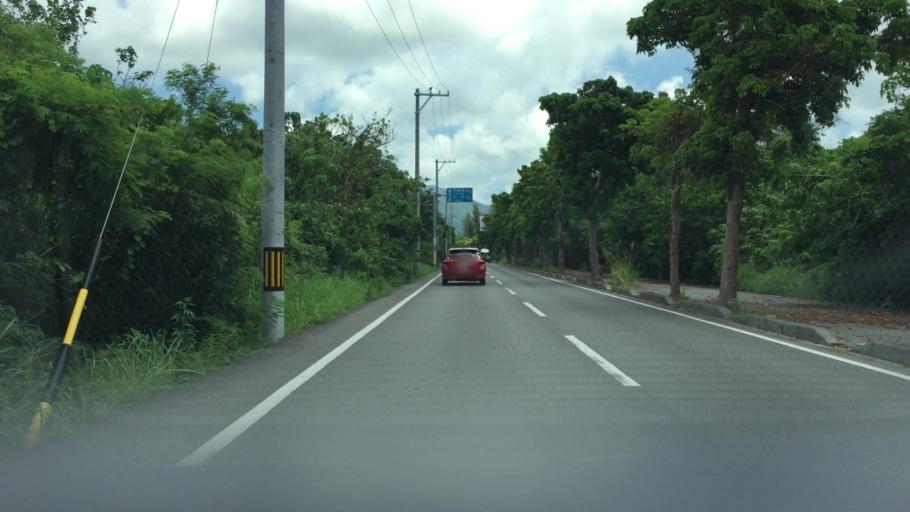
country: JP
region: Okinawa
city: Ishigaki
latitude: 24.3837
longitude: 124.1359
